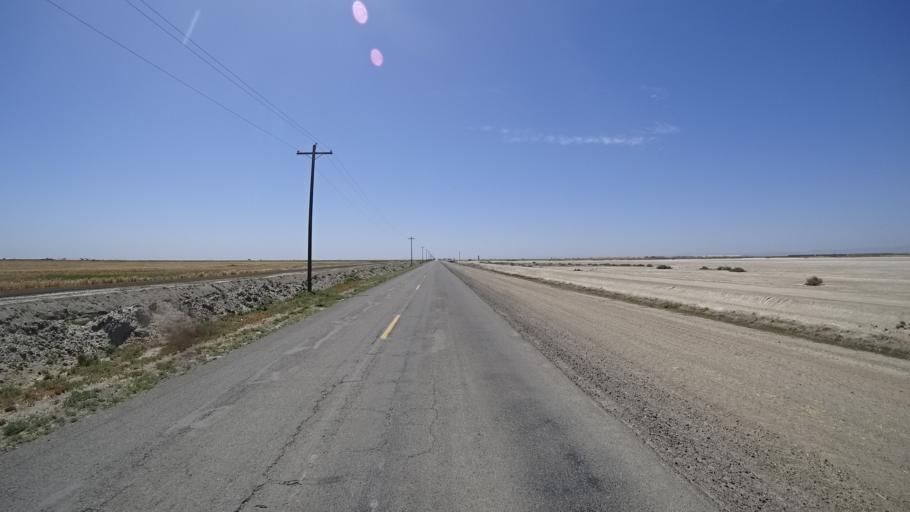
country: US
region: California
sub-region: Kings County
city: Stratford
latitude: 36.1785
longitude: -119.7175
